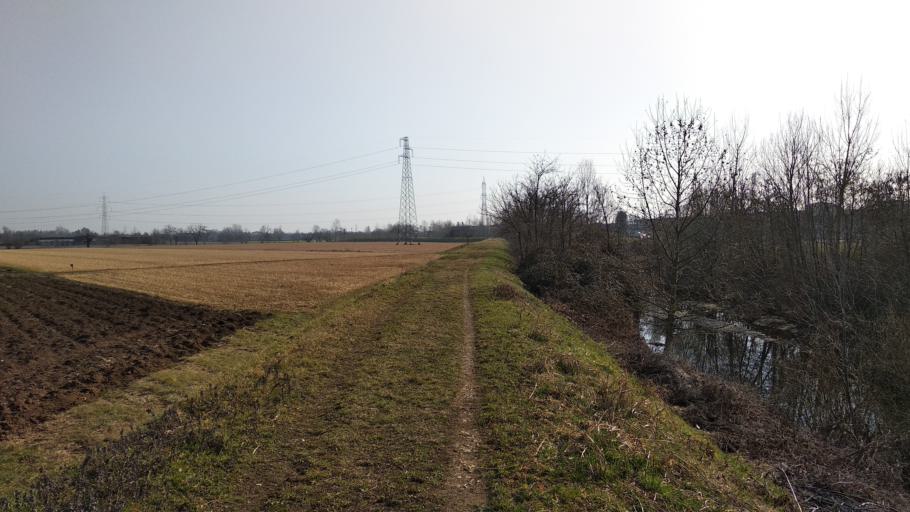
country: IT
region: Veneto
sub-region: Provincia di Vicenza
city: Motta
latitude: 45.5931
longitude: 11.4986
